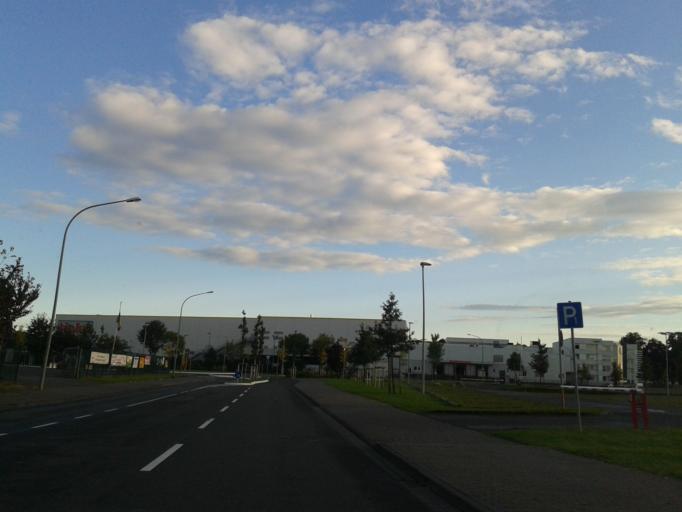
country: DE
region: North Rhine-Westphalia
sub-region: Regierungsbezirk Detmold
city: Paderborn
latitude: 51.7327
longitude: 8.7152
